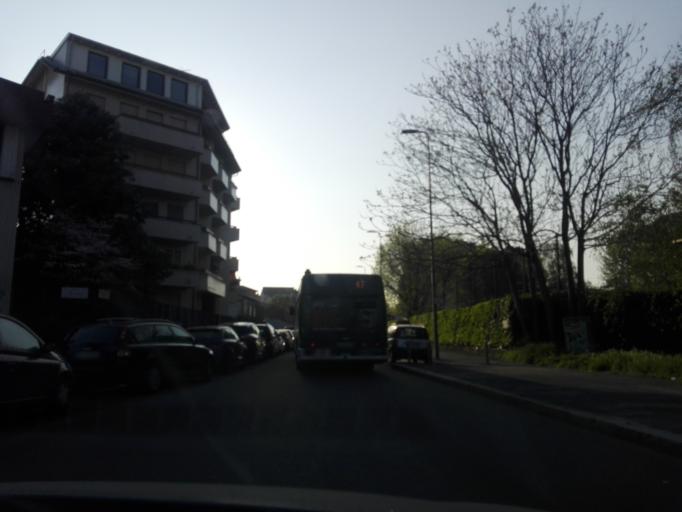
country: IT
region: Lombardy
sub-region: Citta metropolitana di Milano
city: Milano
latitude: 45.4437
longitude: 9.1589
